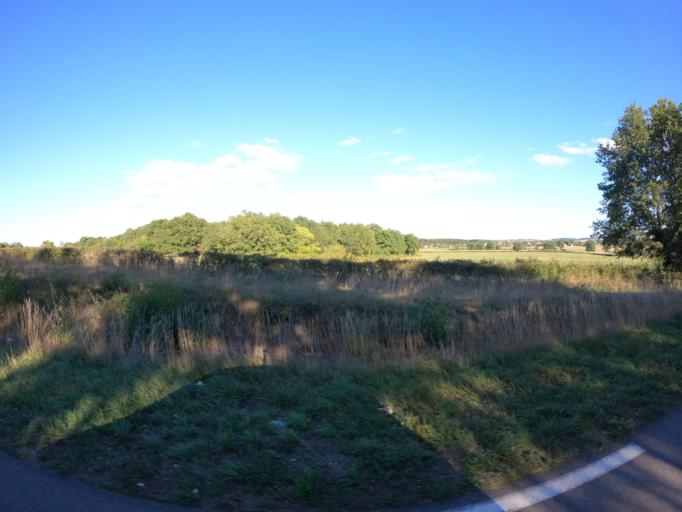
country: FR
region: Bourgogne
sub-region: Departement de Saone-et-Loire
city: Montchanin
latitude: 46.7417
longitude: 4.4451
